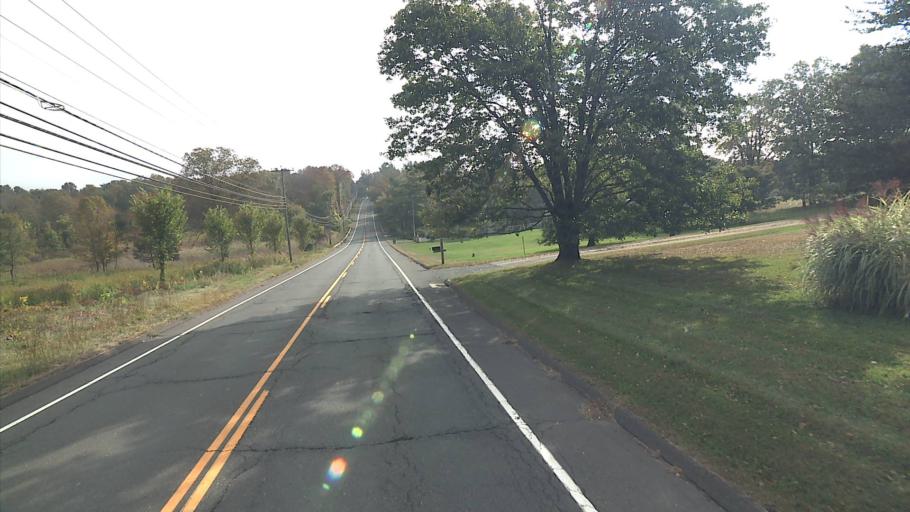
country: US
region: Connecticut
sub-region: Fairfield County
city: Newtown
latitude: 41.4188
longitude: -73.3359
